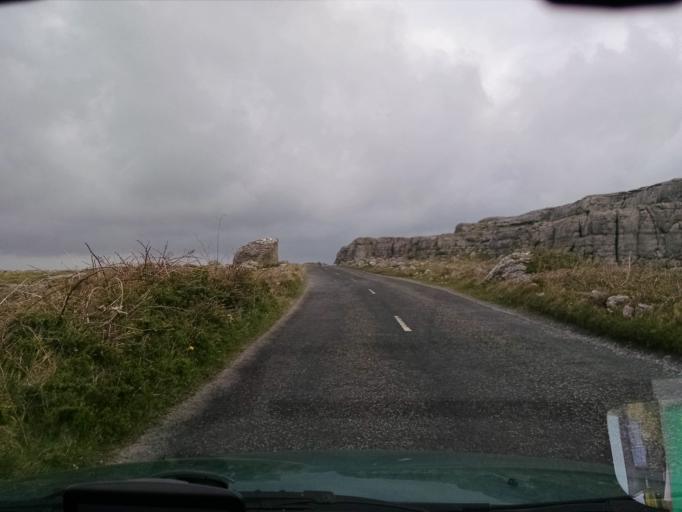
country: IE
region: Connaught
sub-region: County Galway
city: Bearna
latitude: 53.0654
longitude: -9.3593
